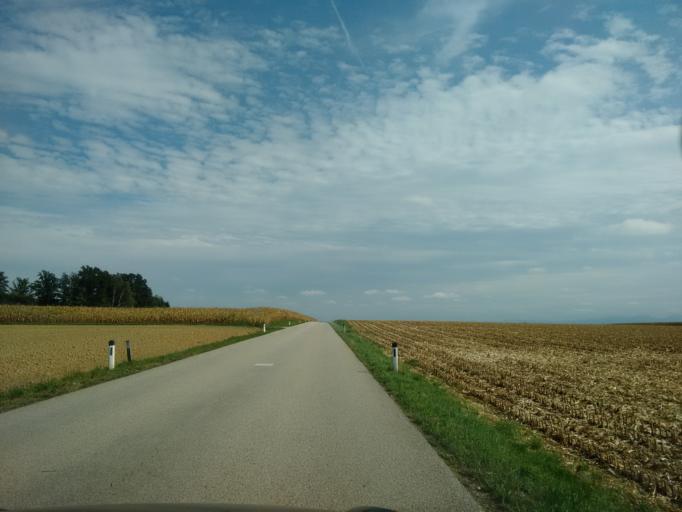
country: AT
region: Upper Austria
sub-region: Wels-Land
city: Marchtrenk
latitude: 48.1229
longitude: 14.1180
